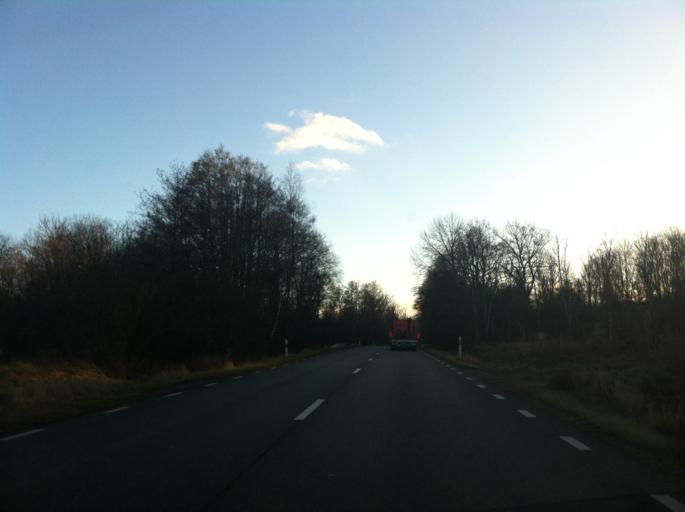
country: SE
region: Skane
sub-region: Hassleholms Kommun
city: Hassleholm
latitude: 56.1831
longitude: 13.8493
